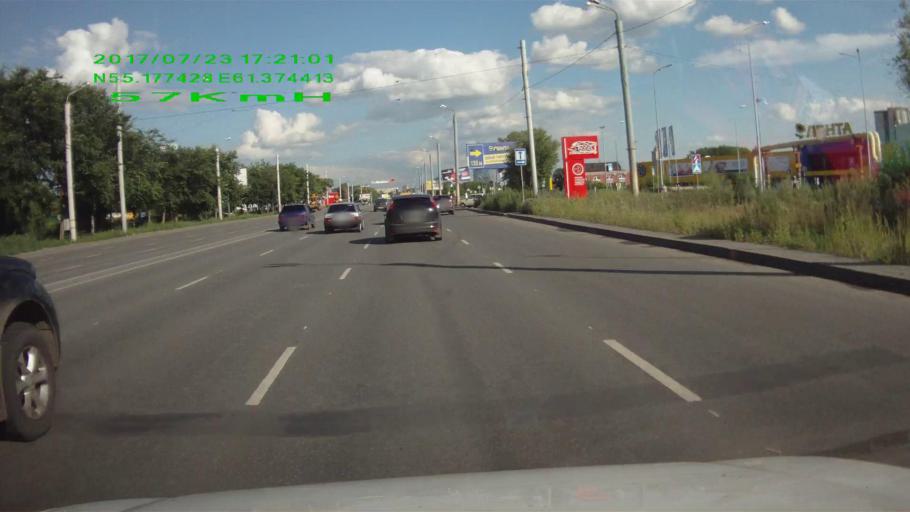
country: RU
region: Chelyabinsk
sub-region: Gorod Chelyabinsk
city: Chelyabinsk
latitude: 55.1772
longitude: 61.3750
